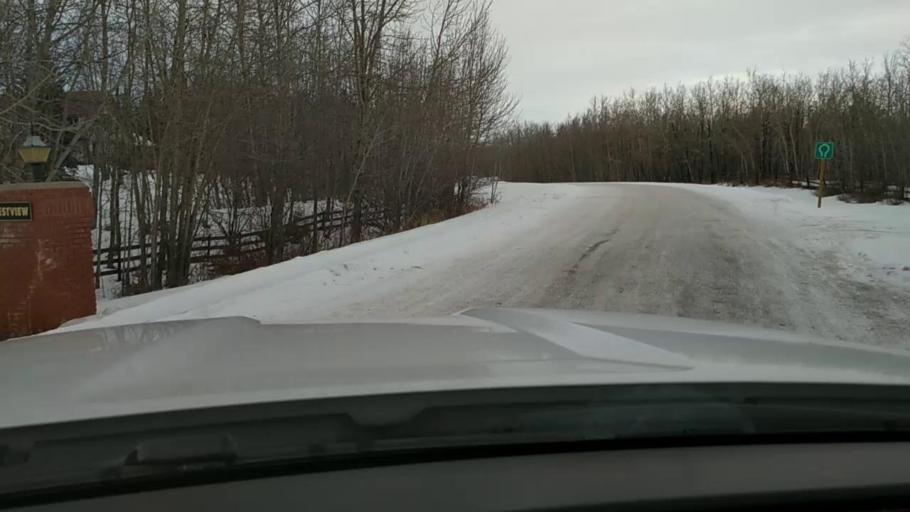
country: CA
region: Alberta
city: Calgary
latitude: 51.1833
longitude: -114.2525
